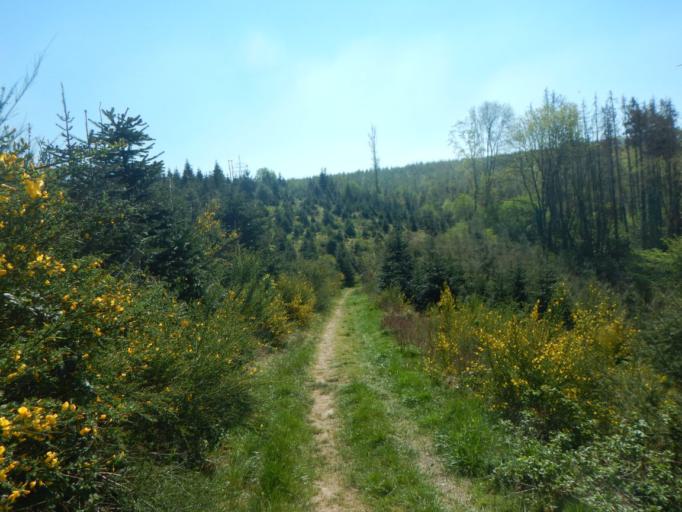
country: LU
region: Diekirch
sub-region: Canton de Diekirch
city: Bourscheid
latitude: 49.9144
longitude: 6.0967
